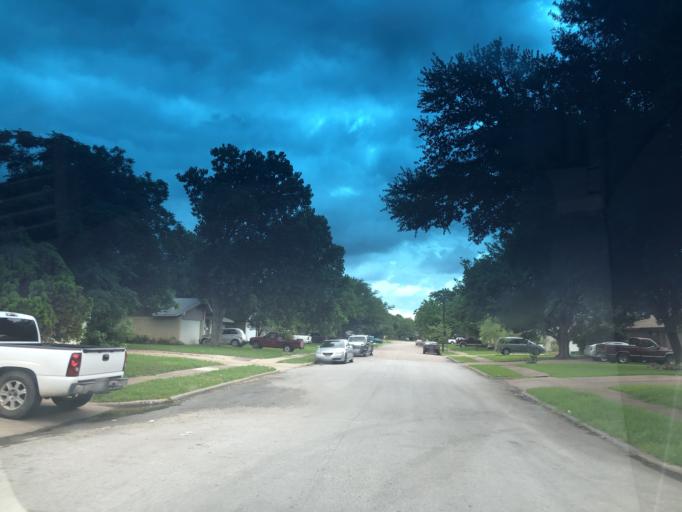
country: US
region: Texas
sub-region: Dallas County
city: Grand Prairie
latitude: 32.7057
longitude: -97.0083
